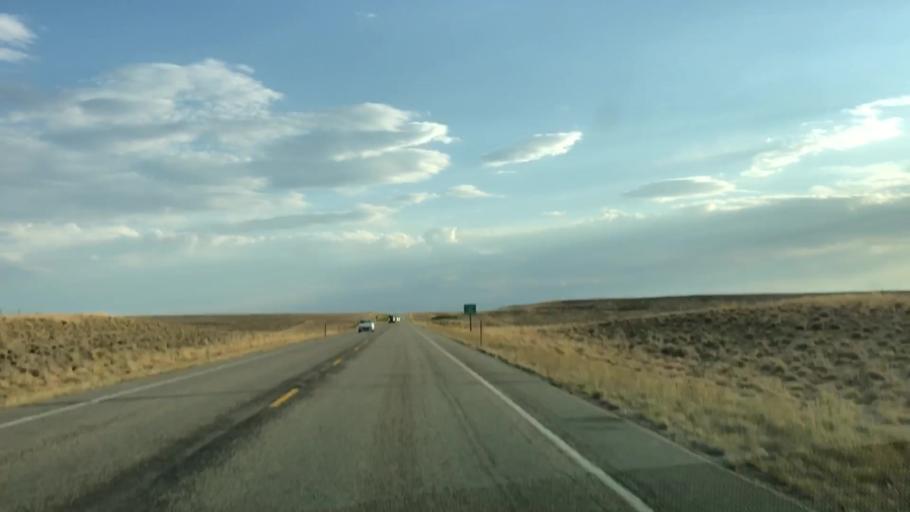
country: US
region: Wyoming
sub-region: Sweetwater County
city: North Rock Springs
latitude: 42.2113
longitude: -109.4725
